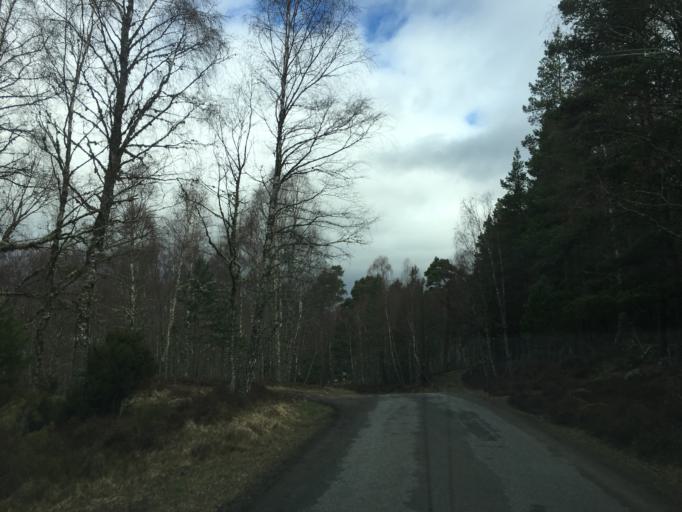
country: GB
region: Scotland
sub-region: Highland
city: Aviemore
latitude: 57.1074
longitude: -3.9206
